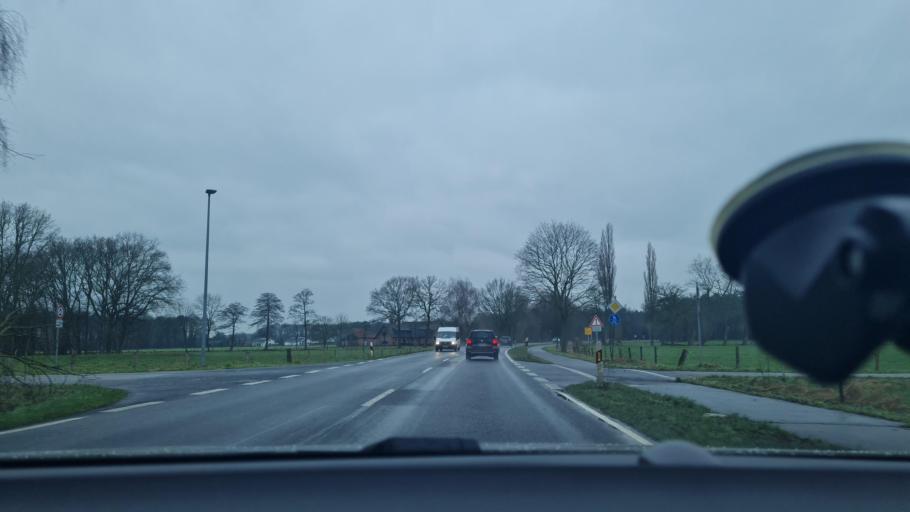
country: DE
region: North Rhine-Westphalia
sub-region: Regierungsbezirk Dusseldorf
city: Hunxe
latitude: 51.6738
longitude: 6.7425
